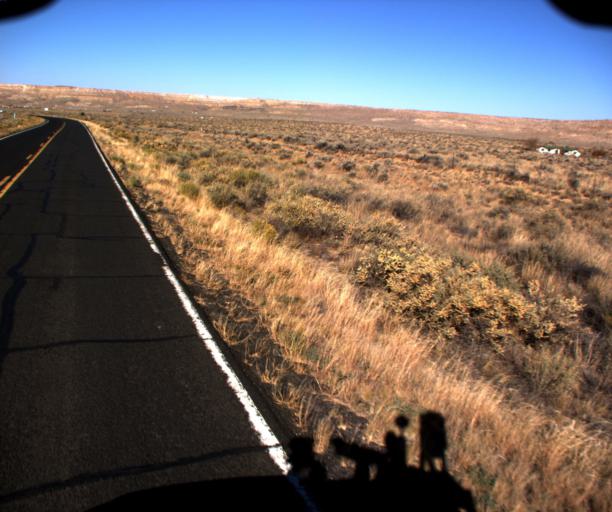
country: US
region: Arizona
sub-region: Navajo County
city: First Mesa
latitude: 35.8416
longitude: -110.3232
